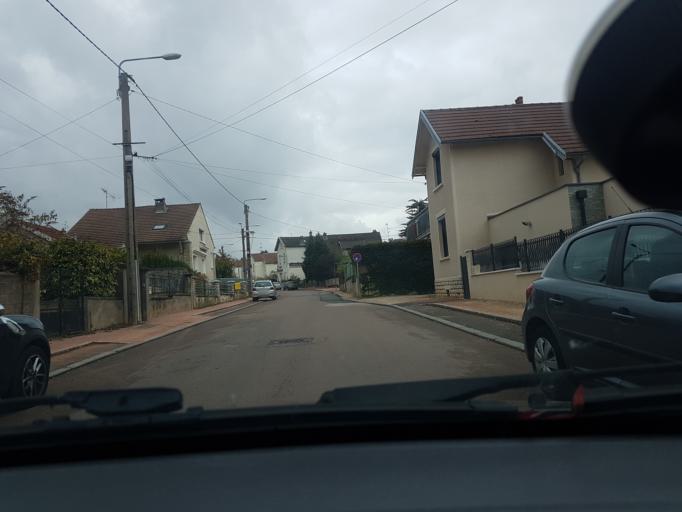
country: FR
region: Bourgogne
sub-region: Departement de la Cote-d'Or
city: Longvic
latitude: 47.3130
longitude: 5.0615
